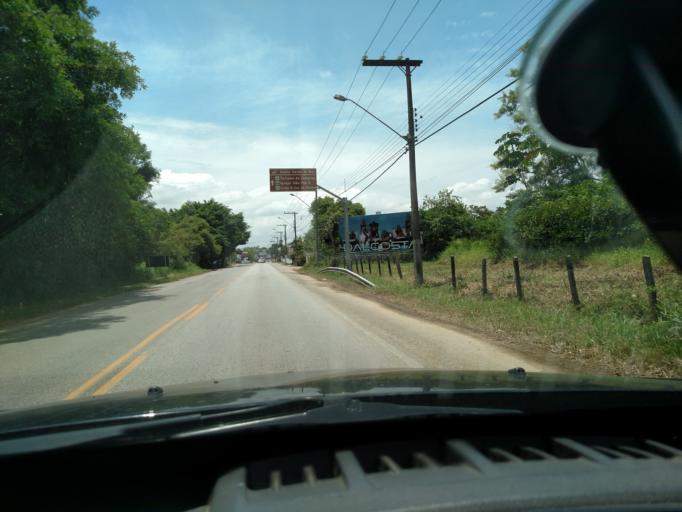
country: BR
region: Santa Catarina
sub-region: Gaspar
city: Gaspar
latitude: -26.9063
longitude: -48.8419
